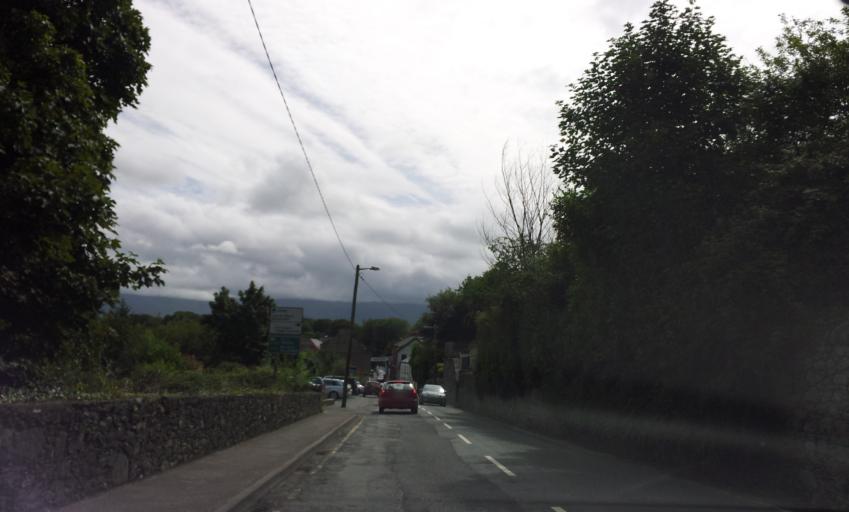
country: IE
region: Munster
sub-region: Ciarrai
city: Killorglin
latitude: 52.1080
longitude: -9.7853
